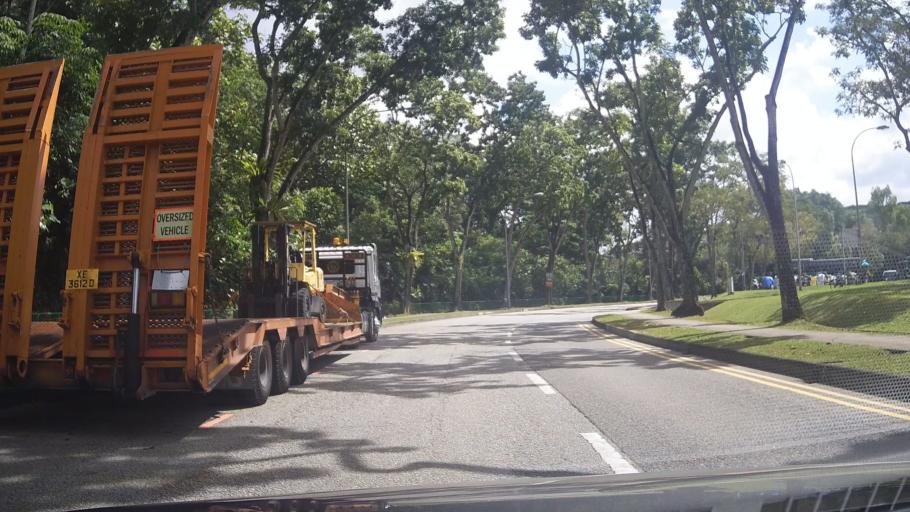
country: MY
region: Johor
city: Johor Bahru
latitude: 1.4491
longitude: 103.7760
